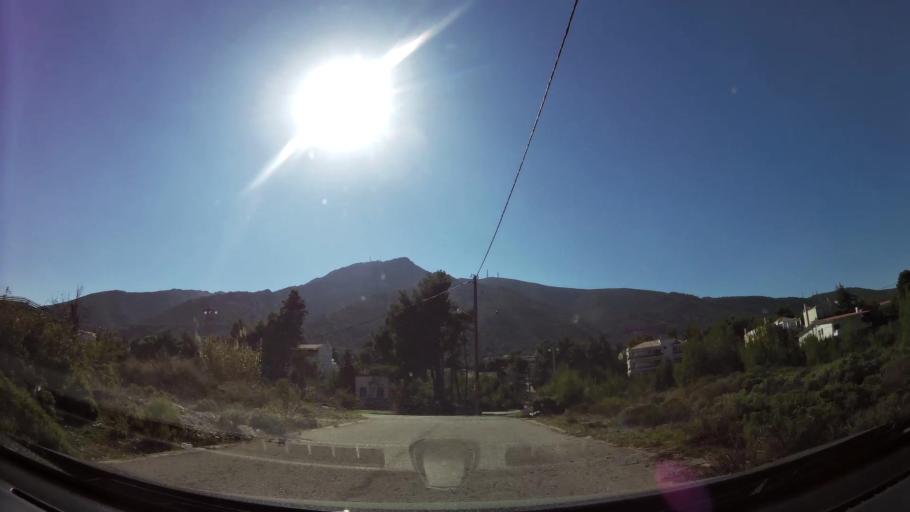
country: GR
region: Attica
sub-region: Nomarchia Anatolikis Attikis
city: Dionysos
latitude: 38.0975
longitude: 23.8896
